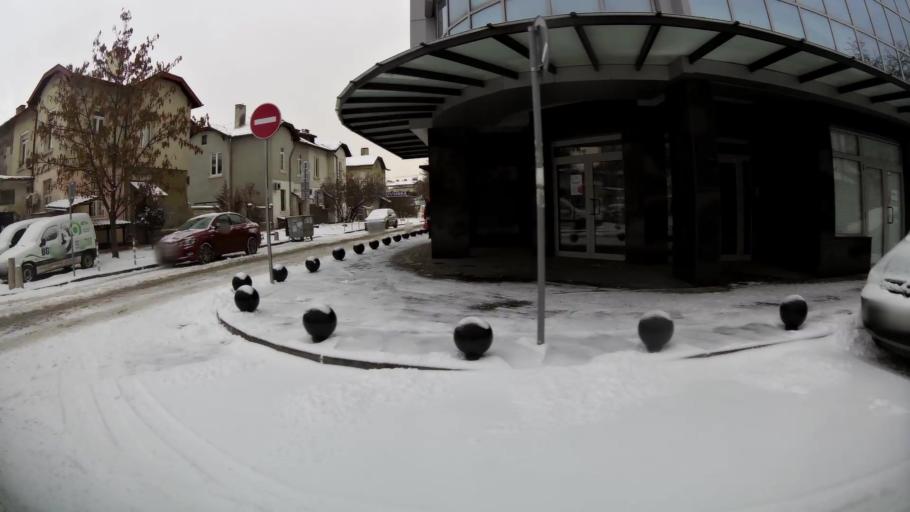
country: BG
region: Sofia-Capital
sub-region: Stolichna Obshtina
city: Sofia
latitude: 42.7050
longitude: 23.3096
